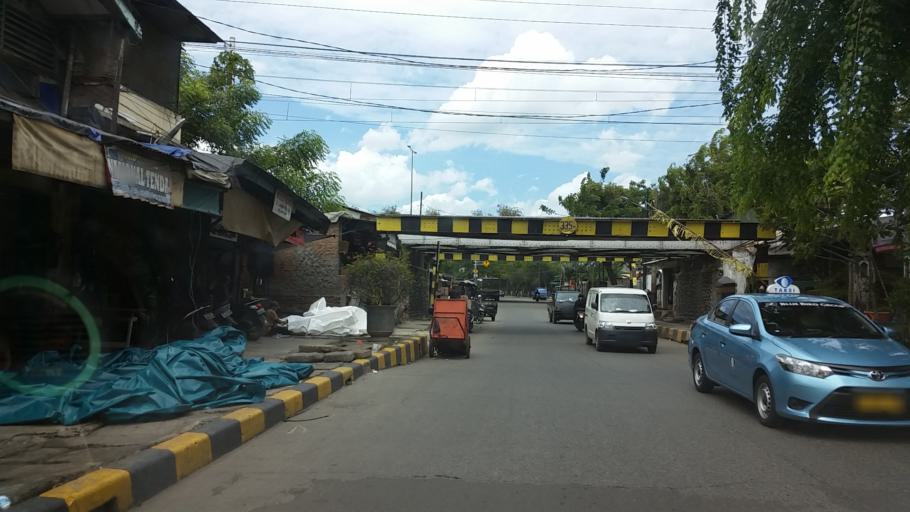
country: ID
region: Jakarta Raya
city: Jakarta
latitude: -6.1307
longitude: 106.8120
